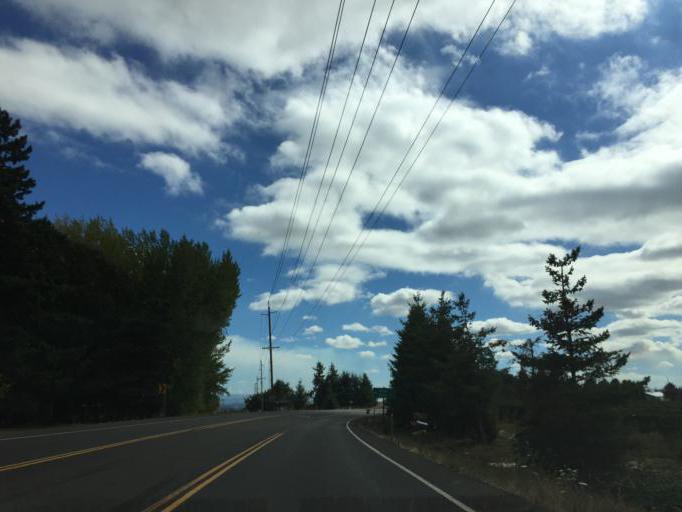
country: US
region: Oregon
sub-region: Marion County
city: Mount Angel
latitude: 45.1129
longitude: -122.7881
